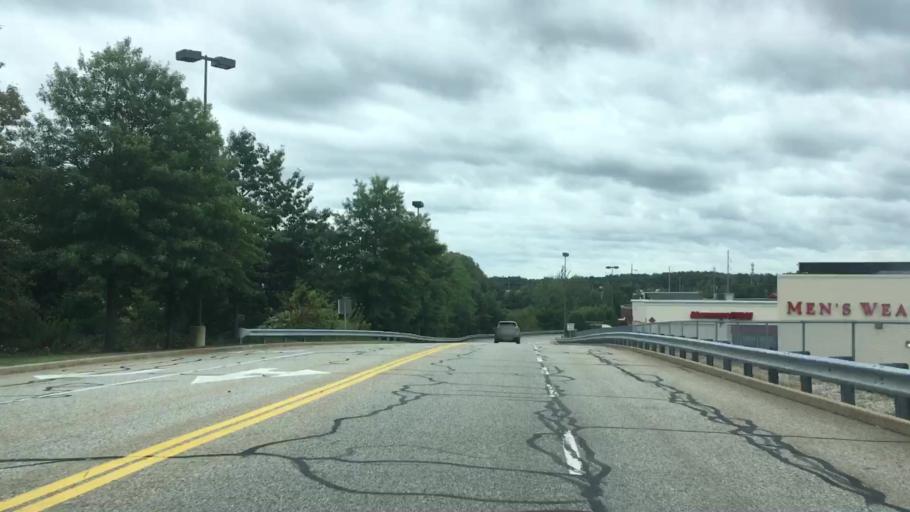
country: US
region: Maine
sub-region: Cumberland County
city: South Portland Gardens
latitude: 43.6363
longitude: -70.3449
